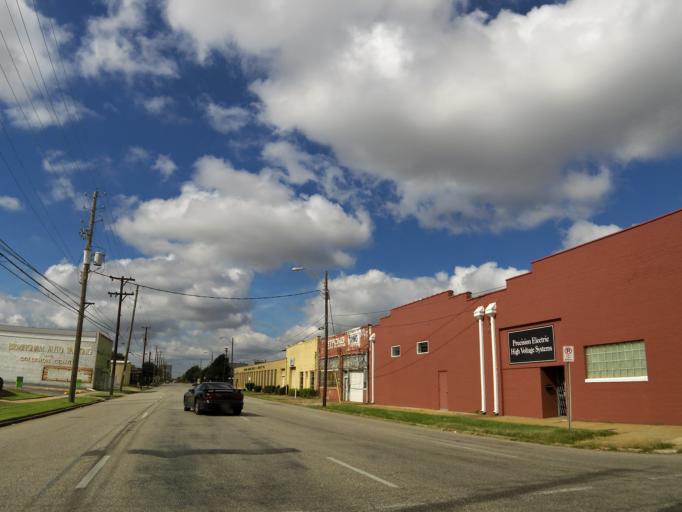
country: US
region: Alabama
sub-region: Jefferson County
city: Birmingham
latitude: 33.5178
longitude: -86.7861
